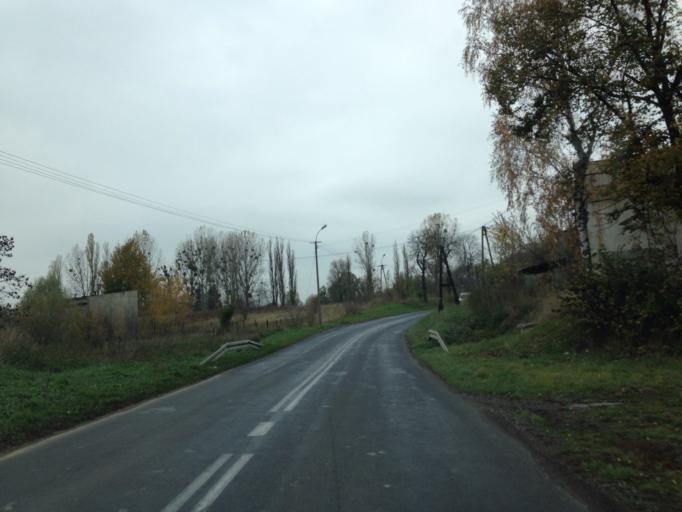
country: PL
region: Kujawsko-Pomorskie
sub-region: Powiat brodnicki
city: Jablonowo Pomorskie
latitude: 53.3421
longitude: 19.2160
